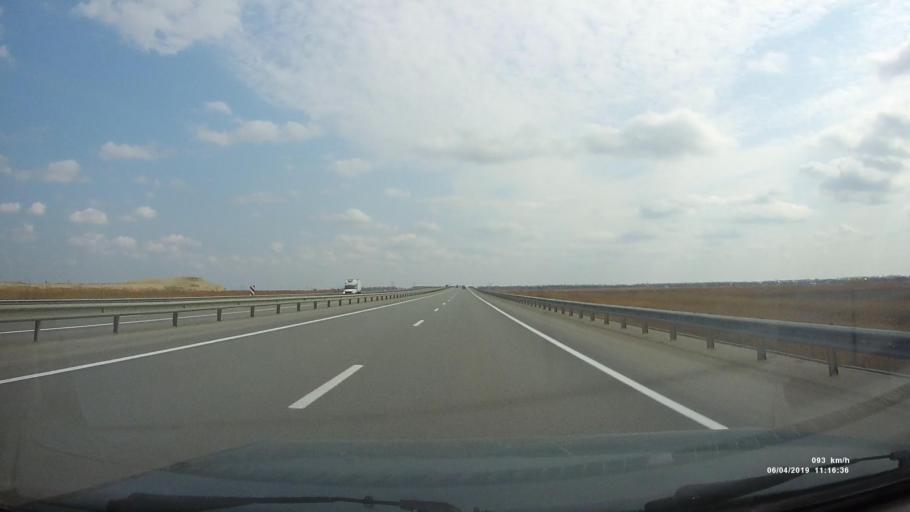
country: RU
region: Rostov
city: Kuleshovka
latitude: 47.0928
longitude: 39.5666
